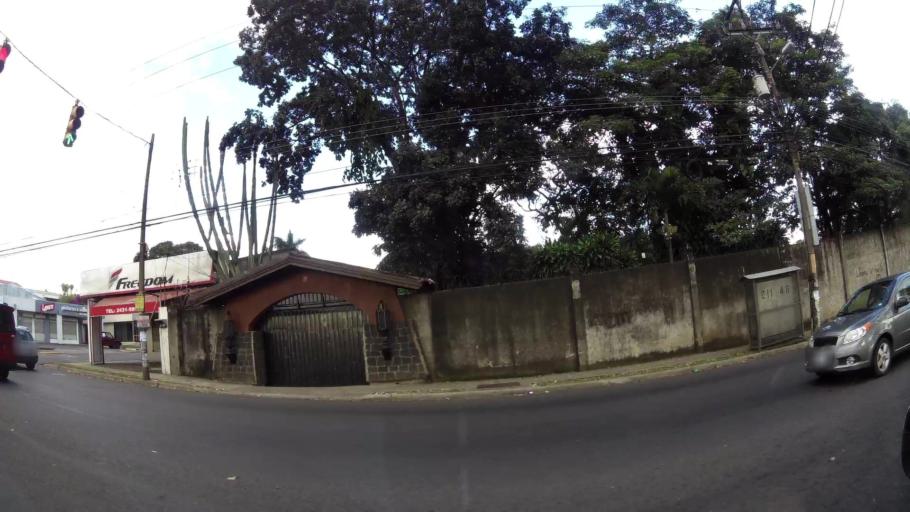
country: CR
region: Alajuela
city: Alajuela
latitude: 10.0087
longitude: -84.2080
